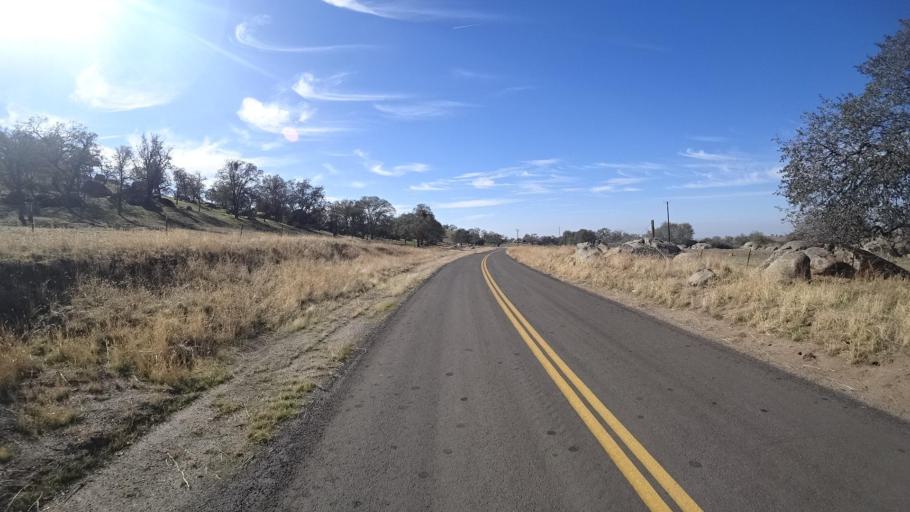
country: US
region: California
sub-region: Kern County
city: Oildale
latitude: 35.6338
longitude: -118.8408
